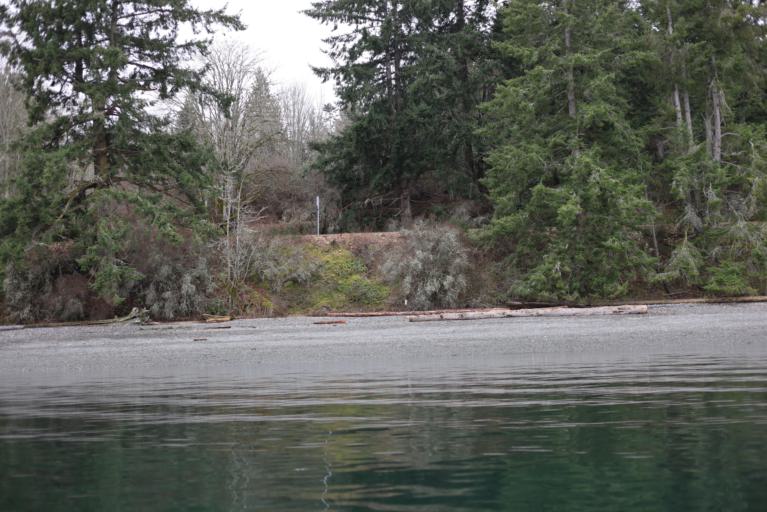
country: CA
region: British Columbia
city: North Saanich
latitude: 48.6331
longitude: -123.5302
